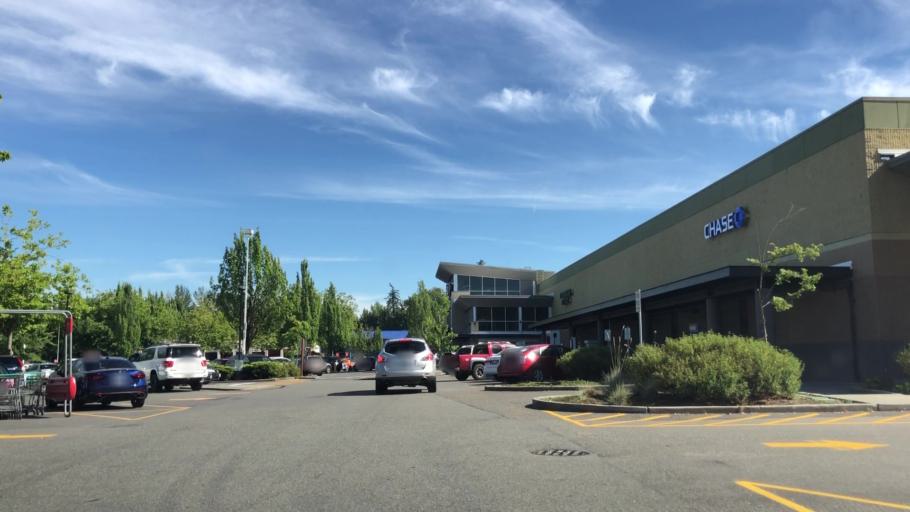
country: US
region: Washington
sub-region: King County
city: Kingsgate
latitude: 47.7089
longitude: -122.1840
